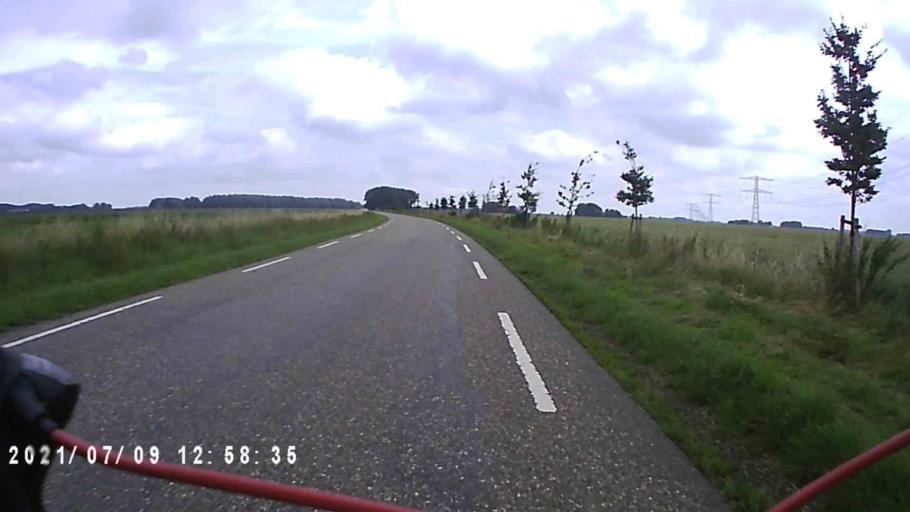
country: NL
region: Groningen
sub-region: Gemeente  Oldambt
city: Winschoten
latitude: 53.1295
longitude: 7.0644
